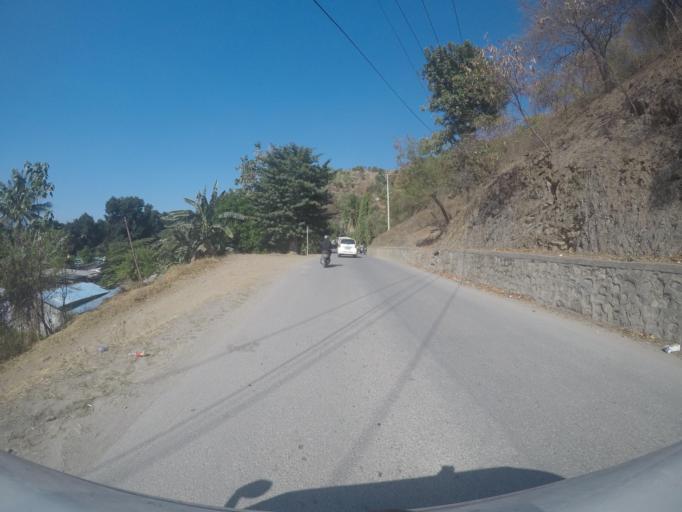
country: TL
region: Dili
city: Dili
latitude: -8.5685
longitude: 125.5466
